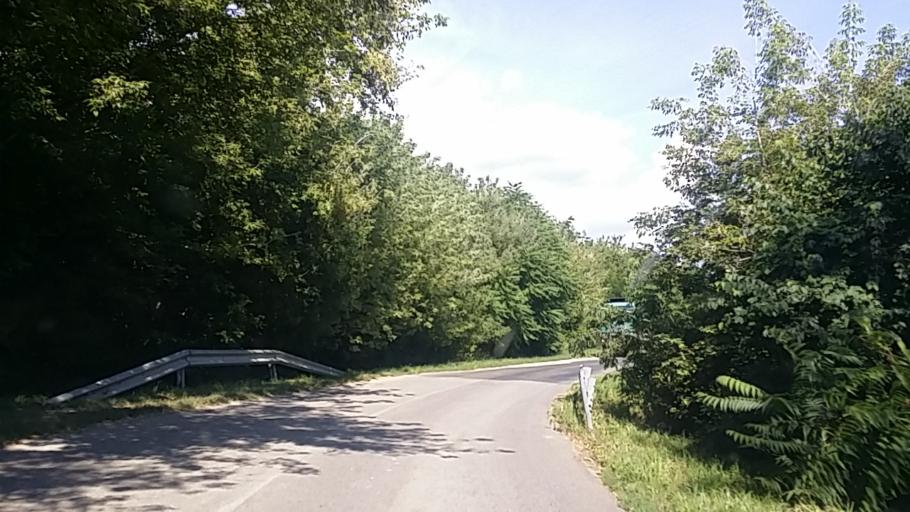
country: HU
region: Tolna
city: Hogyesz
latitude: 46.5263
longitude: 18.4278
